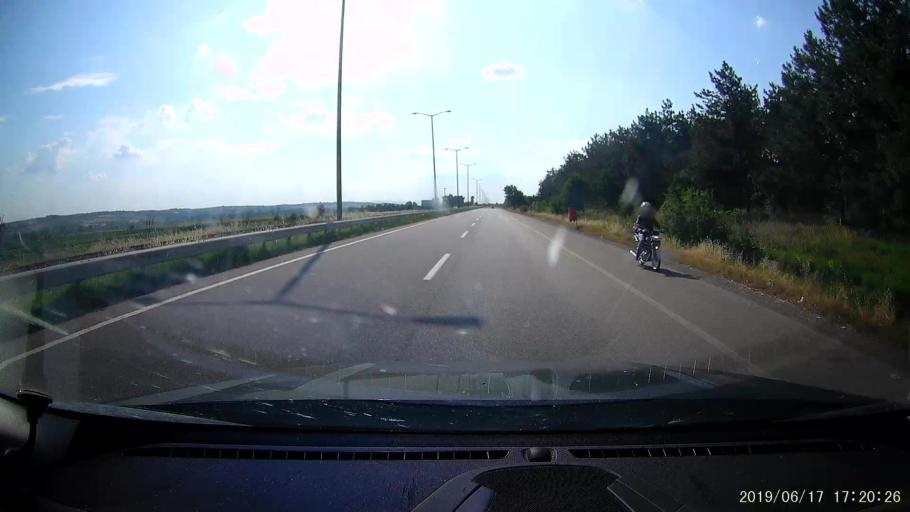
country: GR
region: East Macedonia and Thrace
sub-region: Nomos Evrou
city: Rizia
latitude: 41.7019
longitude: 26.4142
